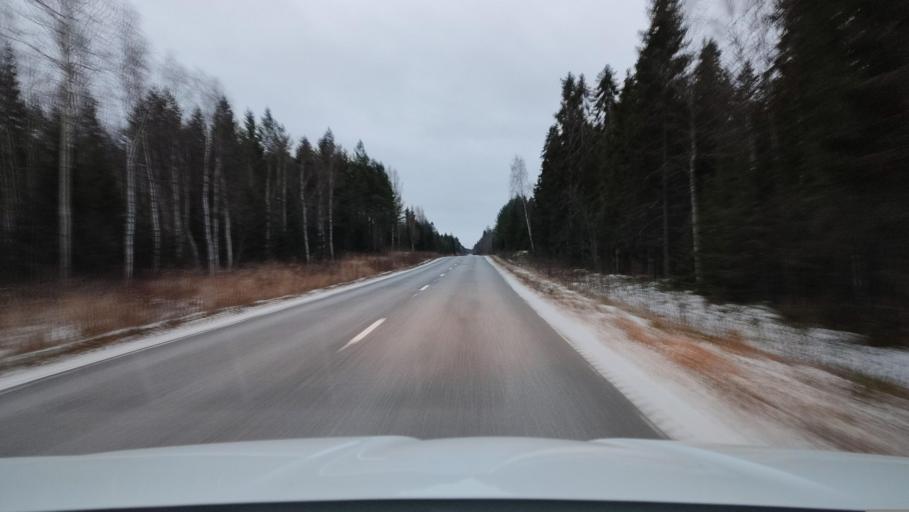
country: FI
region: Ostrobothnia
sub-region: Vaasa
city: Replot
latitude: 63.2605
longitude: 21.3625
